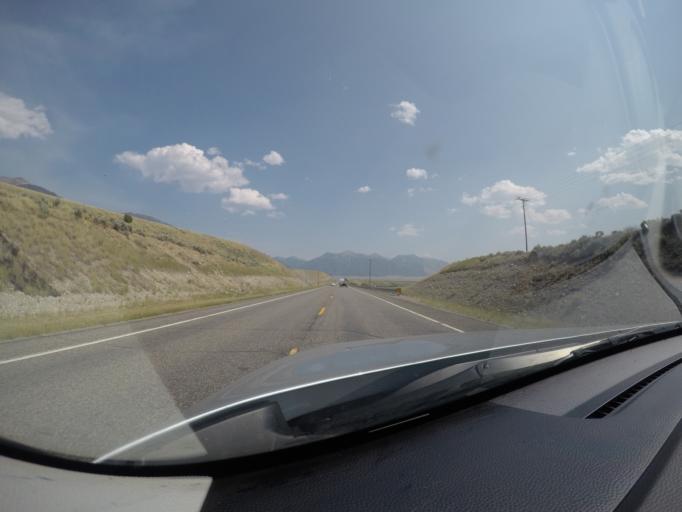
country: US
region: Montana
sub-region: Gallatin County
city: West Yellowstone
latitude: 44.8438
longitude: -111.5227
